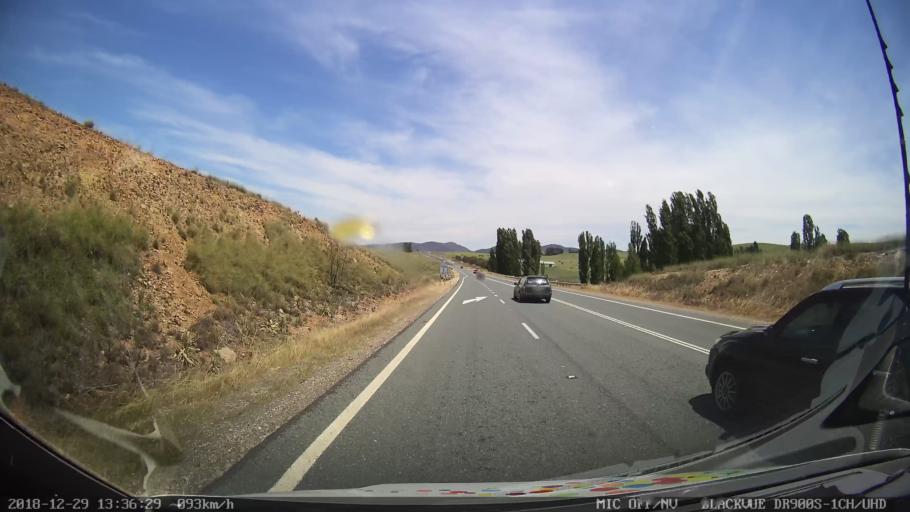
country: AU
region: New South Wales
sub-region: Cooma-Monaro
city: Cooma
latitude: -35.9711
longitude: 149.1406
